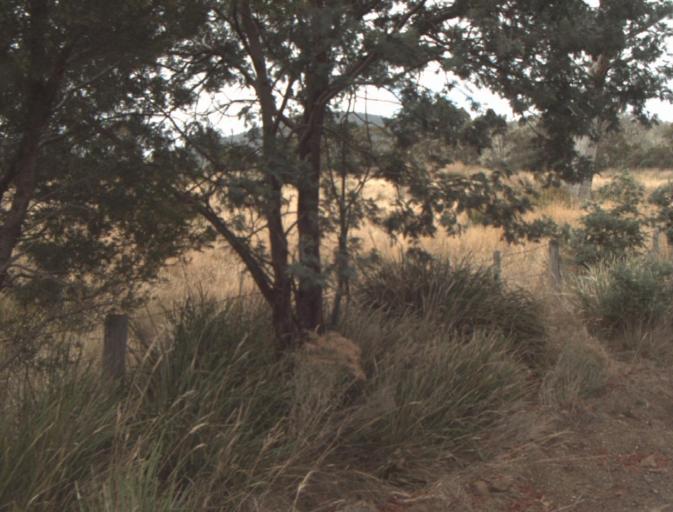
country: AU
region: Tasmania
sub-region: Northern Midlands
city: Evandale
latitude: -41.5049
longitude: 147.3577
